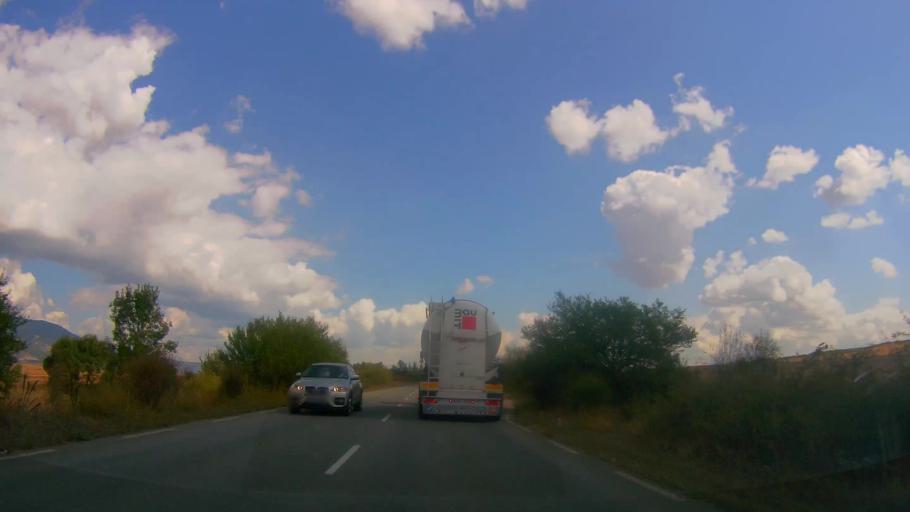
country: BG
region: Sliven
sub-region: Obshtina Tvurditsa
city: Tvurditsa
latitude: 42.6574
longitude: 25.9172
